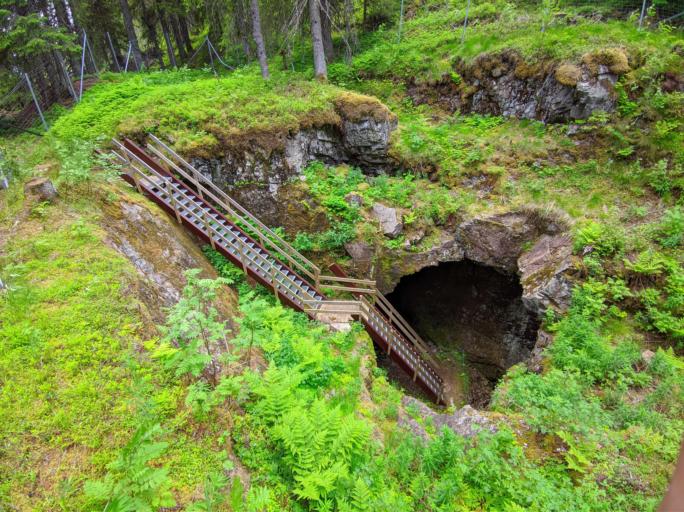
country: NO
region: Akershus
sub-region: Hurdal
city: Hurdal
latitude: 60.5589
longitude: 11.1388
